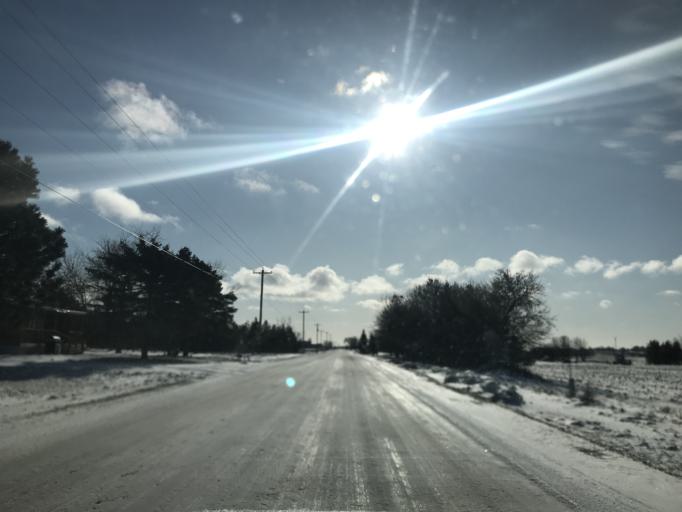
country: US
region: Wisconsin
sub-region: Kewaunee County
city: Luxemburg
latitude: 44.6999
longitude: -87.6206
